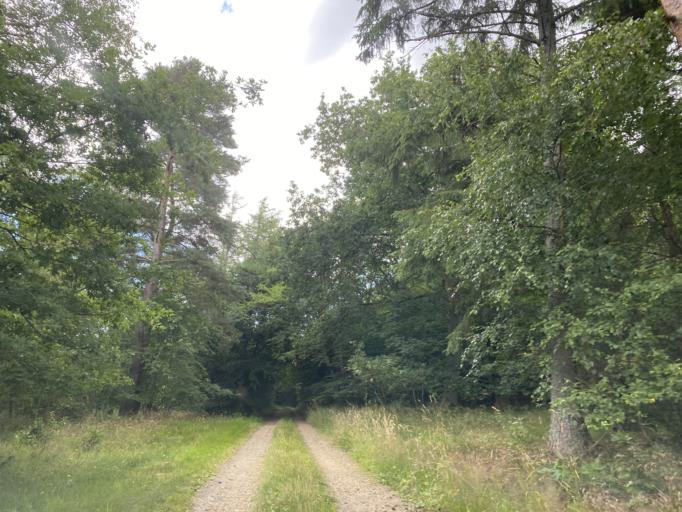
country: DK
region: Central Jutland
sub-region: Viborg Kommune
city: Bjerringbro
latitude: 56.2781
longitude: 9.6560
